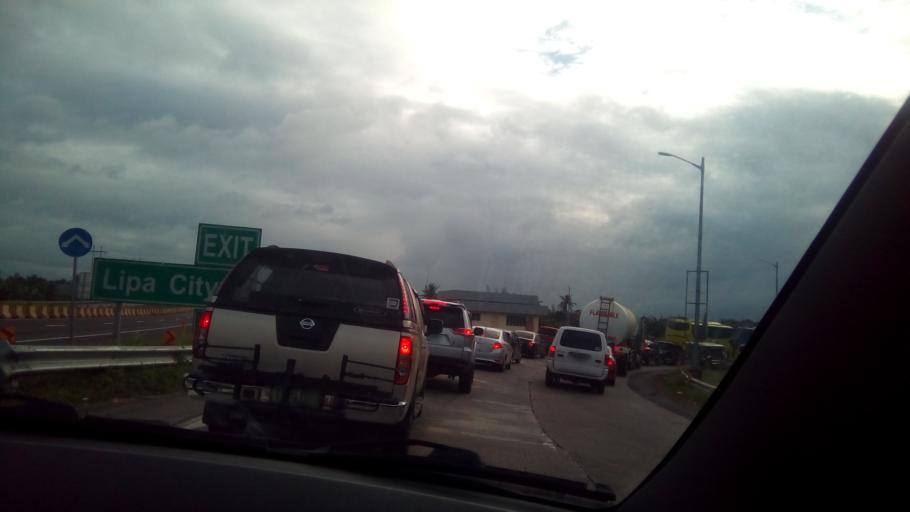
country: PH
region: Calabarzon
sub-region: Province of Batangas
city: Banaybanay
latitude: 13.9401
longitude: 121.1373
